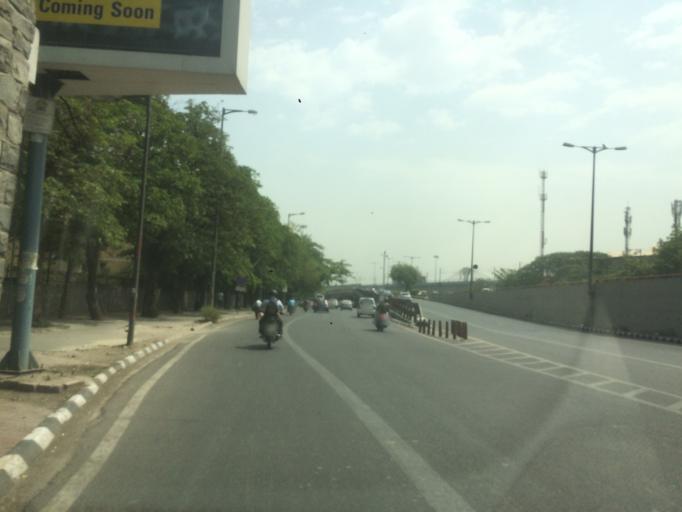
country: IN
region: NCT
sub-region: New Delhi
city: New Delhi
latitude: 28.5633
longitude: 77.2327
